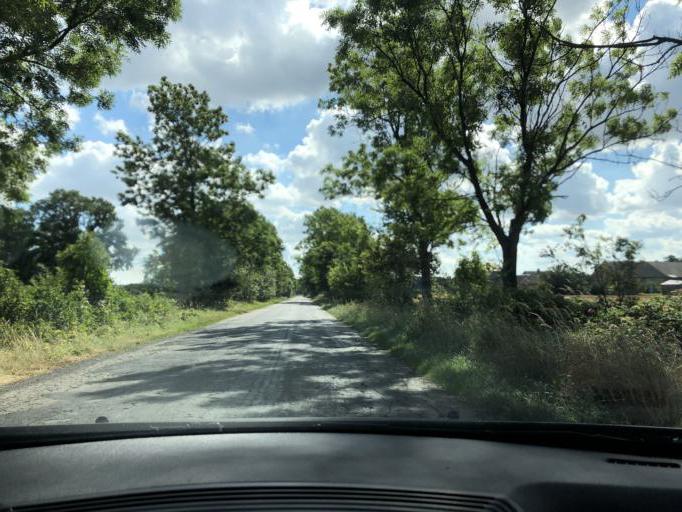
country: PL
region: Lodz Voivodeship
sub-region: Powiat wieruszowski
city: Czastary
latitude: 51.2323
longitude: 18.3528
